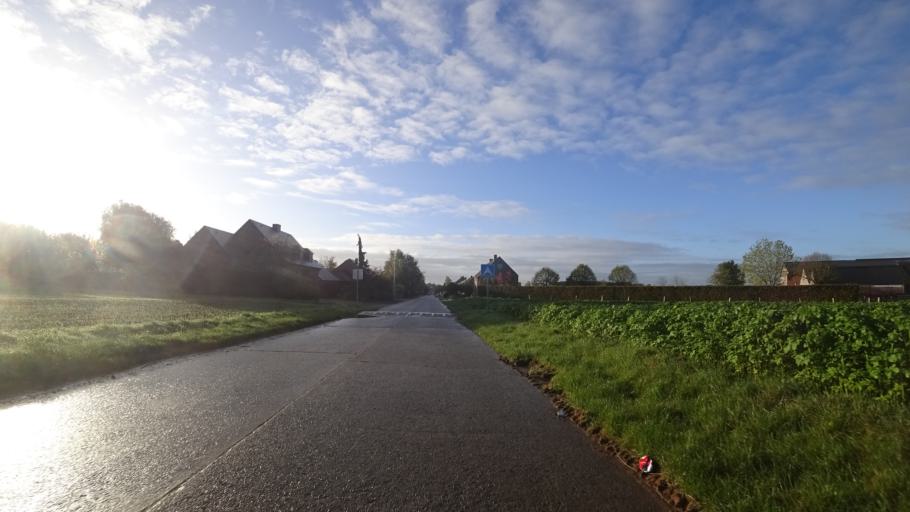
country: BE
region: Wallonia
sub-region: Province de Namur
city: Gembloux
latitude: 50.5231
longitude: 4.7810
